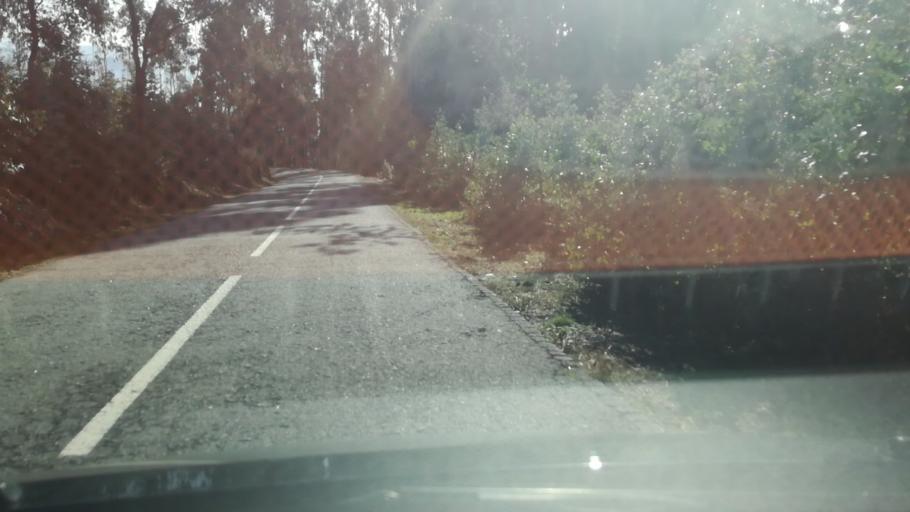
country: PT
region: Braga
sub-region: Braga
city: Braga
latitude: 41.5321
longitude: -8.3561
